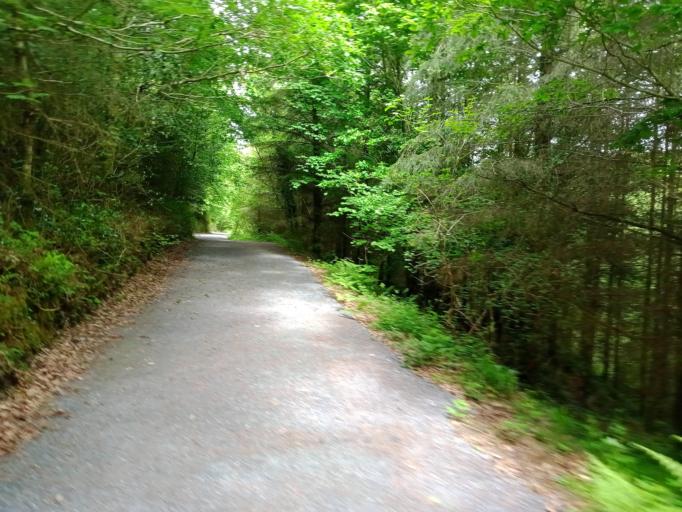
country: IE
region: Leinster
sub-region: Kilkenny
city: Thomastown
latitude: 52.4738
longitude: -7.0465
